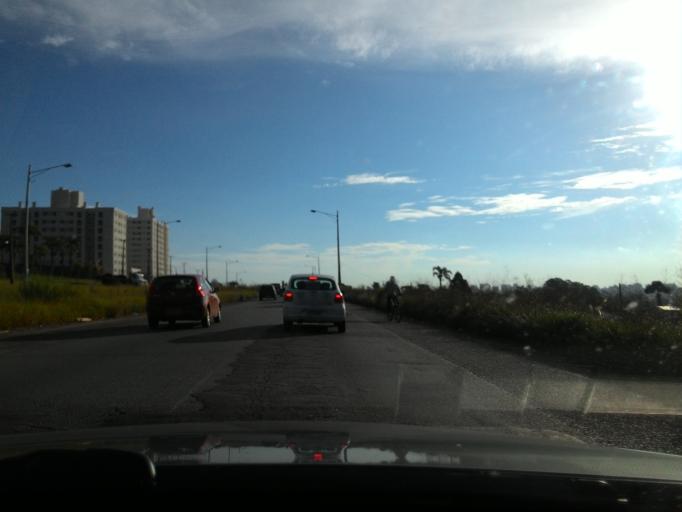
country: BR
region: Parana
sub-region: Pinhais
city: Pinhais
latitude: -25.3951
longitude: -49.2117
